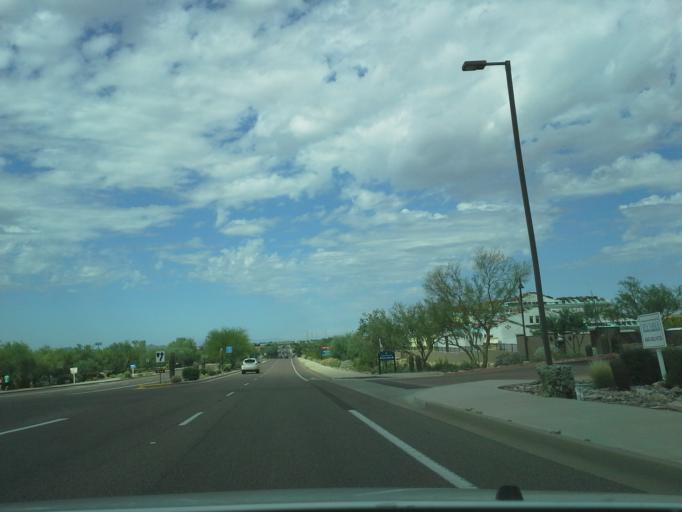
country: US
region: Arizona
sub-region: Maricopa County
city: Paradise Valley
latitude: 33.6402
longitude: -111.8629
